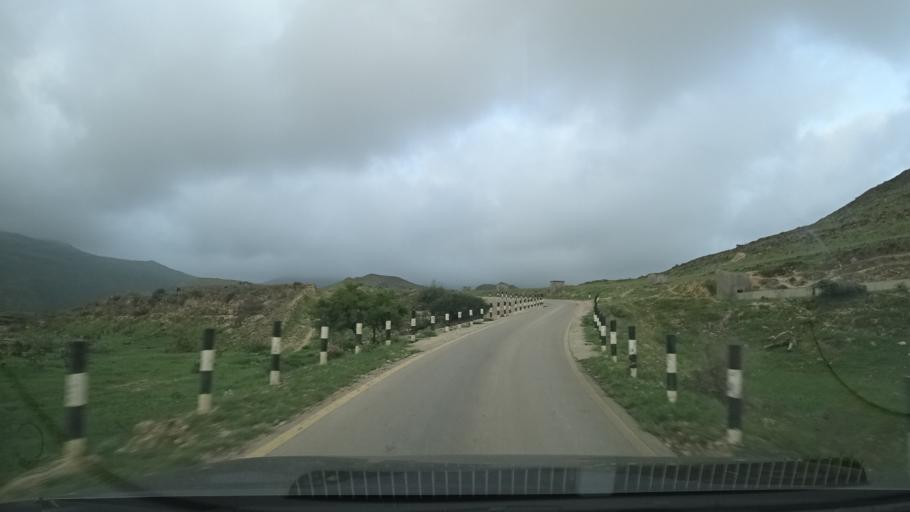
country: OM
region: Zufar
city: Salalah
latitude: 17.1172
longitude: 54.2277
